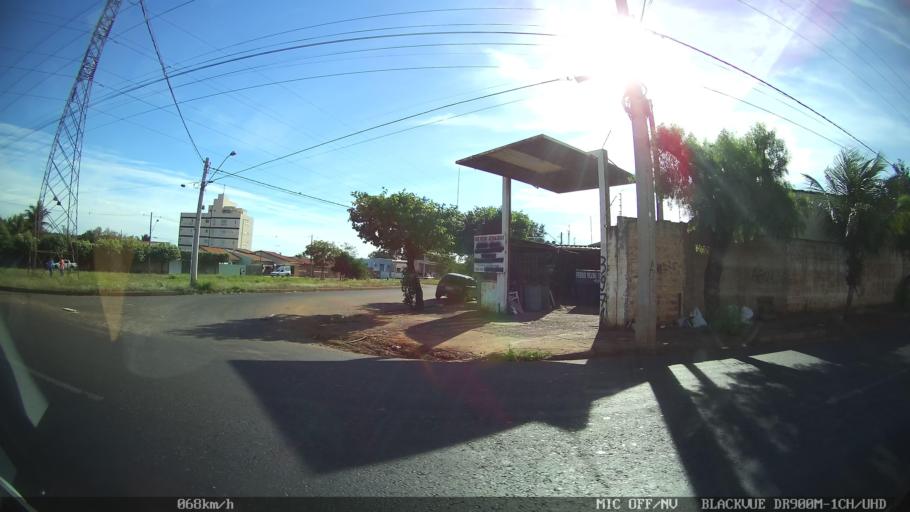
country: BR
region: Sao Paulo
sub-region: Sao Jose Do Rio Preto
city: Sao Jose do Rio Preto
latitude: -20.7709
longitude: -49.3508
